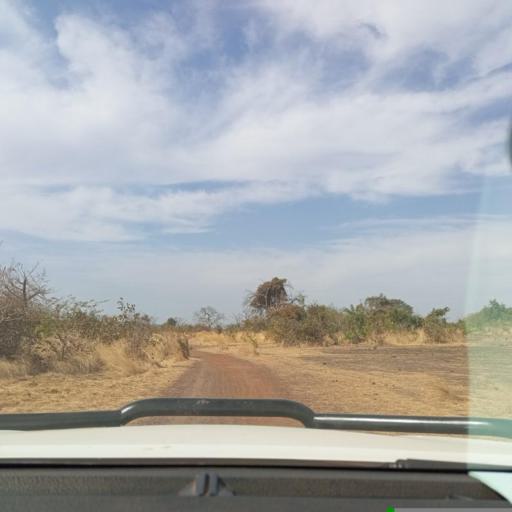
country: ML
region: Koulikoro
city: Kati
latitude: 12.7442
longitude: -8.2491
